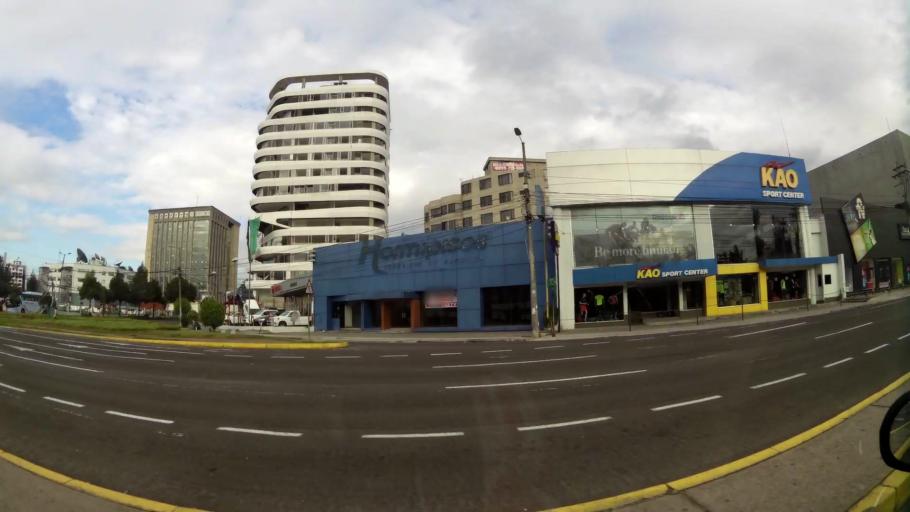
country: EC
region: Pichincha
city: Quito
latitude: -0.1904
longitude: -78.4864
